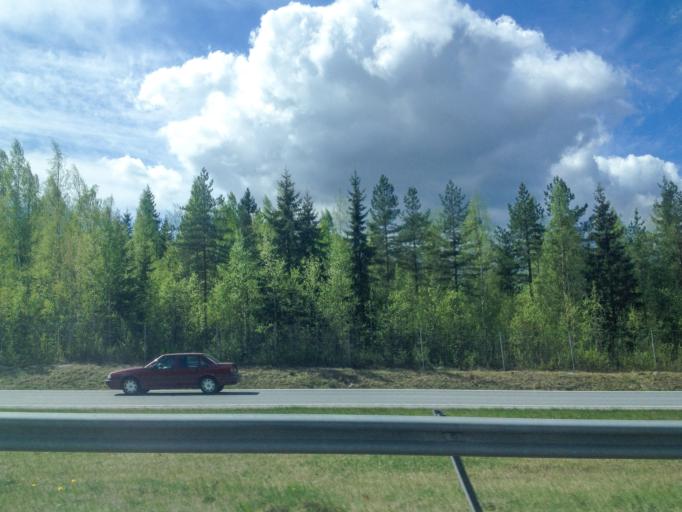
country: FI
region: Pirkanmaa
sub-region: Tampere
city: Lempaeaelae
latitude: 61.2797
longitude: 23.8099
